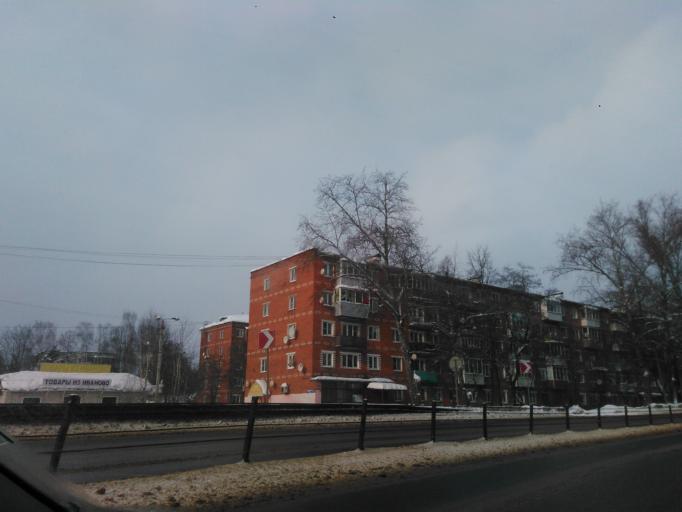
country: RU
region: Moskovskaya
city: Dedenevo
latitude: 56.2377
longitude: 37.5233
